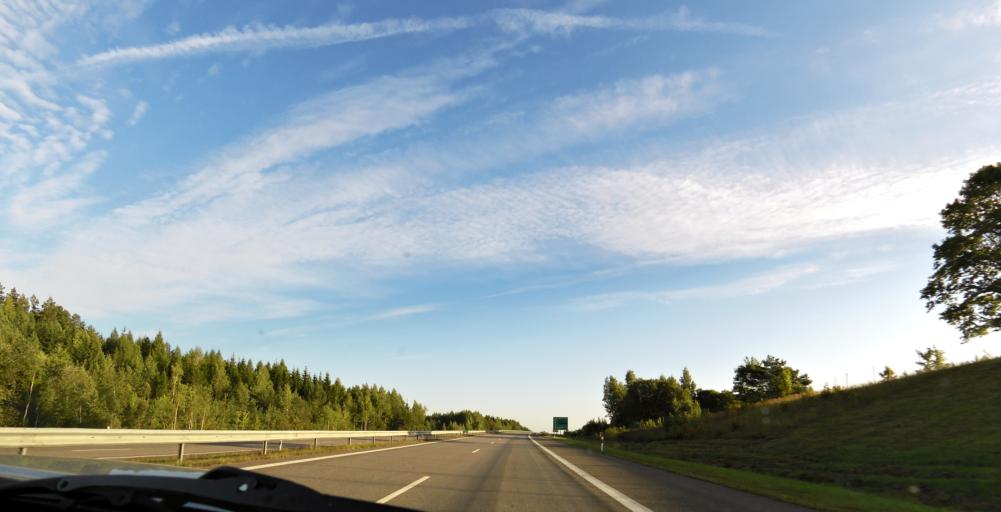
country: LT
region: Vilnius County
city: Ukmerge
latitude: 55.2201
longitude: 24.8166
